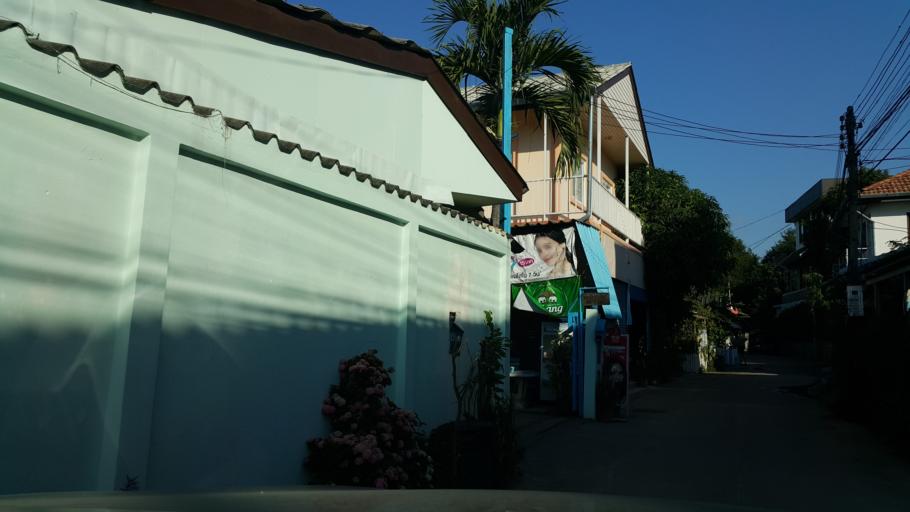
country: TH
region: Chiang Mai
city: Chiang Mai
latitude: 18.7684
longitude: 98.9542
